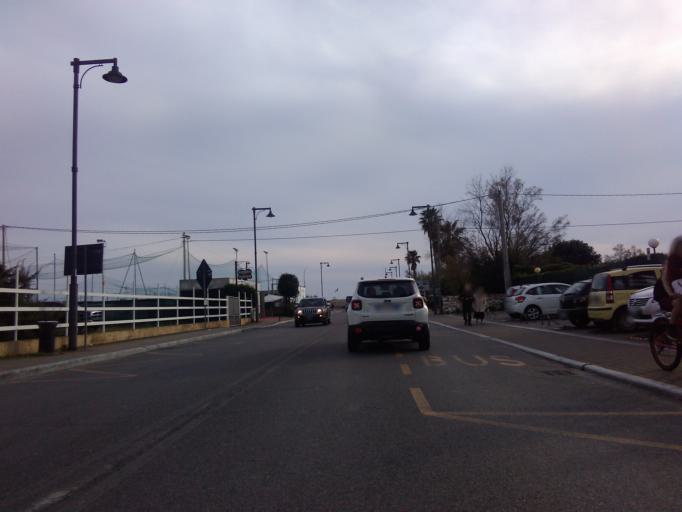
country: IT
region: Tuscany
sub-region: Provincia di Massa-Carrara
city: Massa
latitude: 44.0126
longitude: 10.0943
